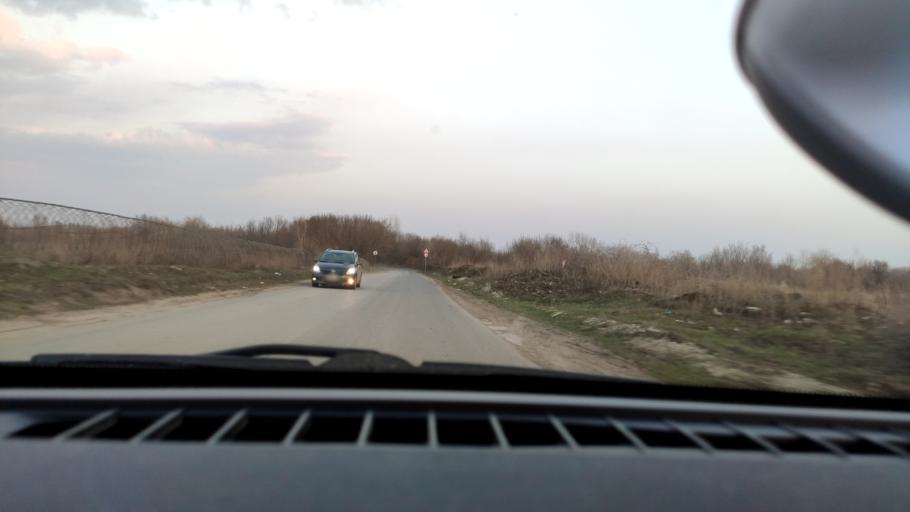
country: RU
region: Samara
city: Smyshlyayevka
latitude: 53.2067
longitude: 50.3126
